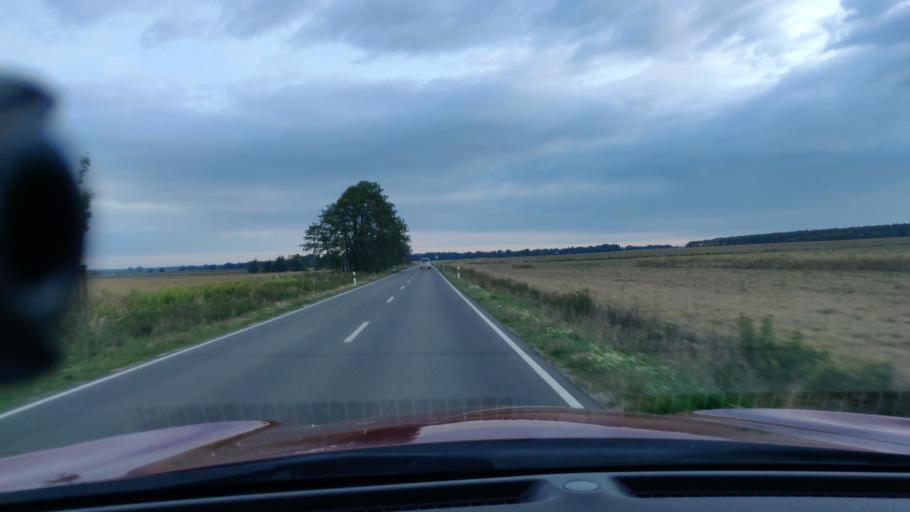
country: DE
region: Saxony
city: Schildau
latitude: 51.4971
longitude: 12.9128
